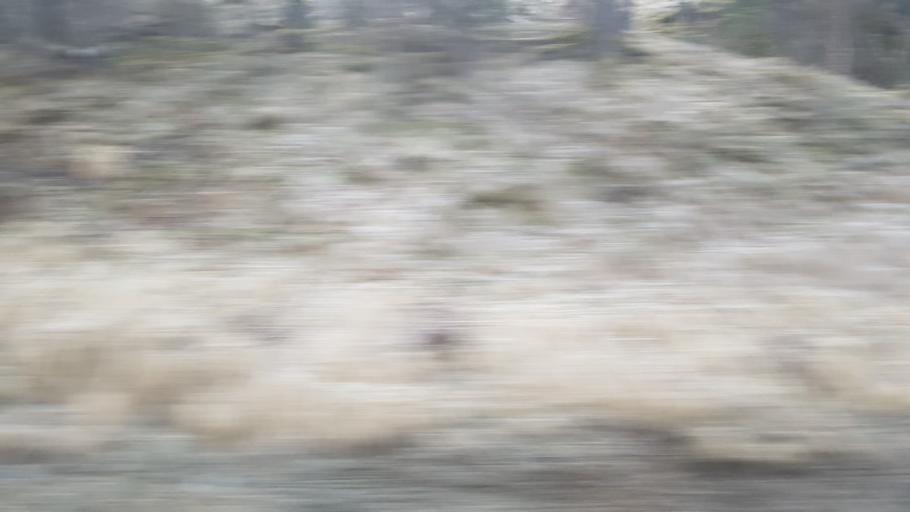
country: NO
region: Nord-Trondelag
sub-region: Stjordal
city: Stjordalshalsen
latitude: 63.5854
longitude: 11.0053
